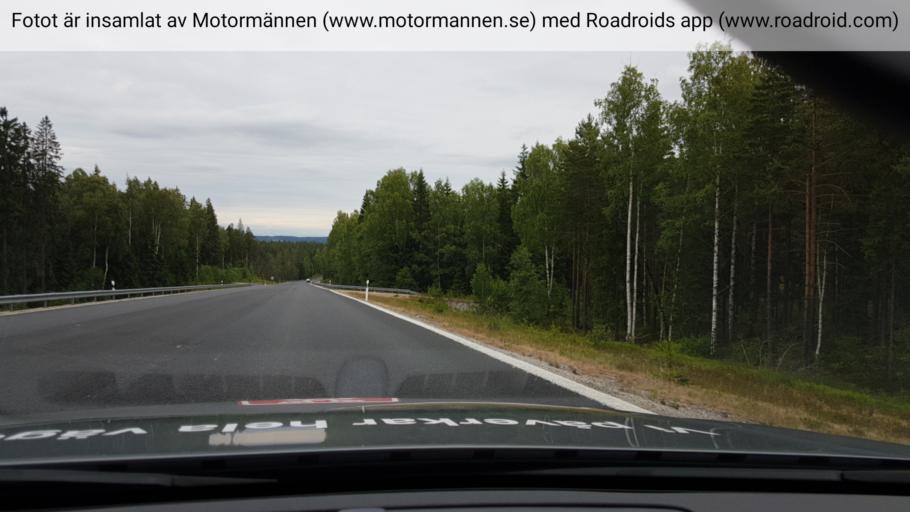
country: SE
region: Vaestmanland
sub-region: Skinnskattebergs Kommun
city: Skinnskatteberg
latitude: 59.8514
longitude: 15.5857
